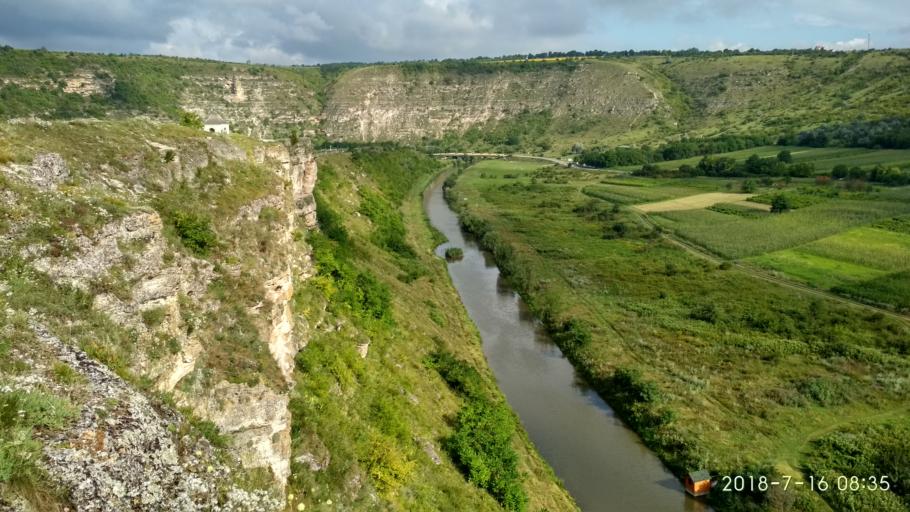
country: MD
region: Telenesti
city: Cocieri
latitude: 47.3020
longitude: 28.9702
